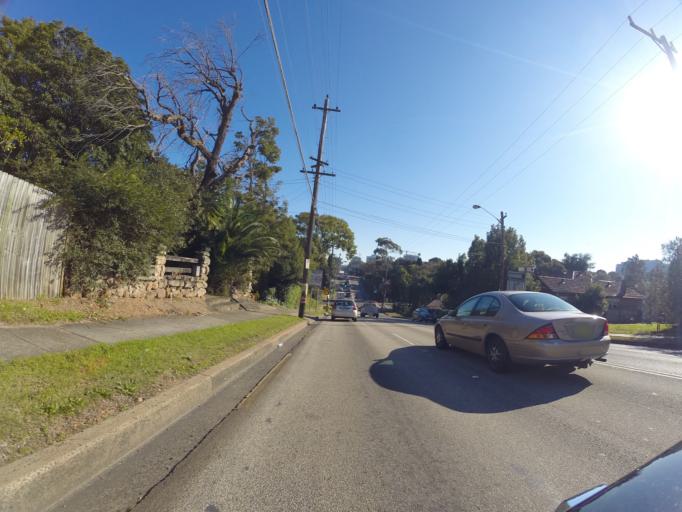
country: AU
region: New South Wales
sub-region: Kogarah
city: Hurstville Grove
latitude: -33.9713
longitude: 151.0993
